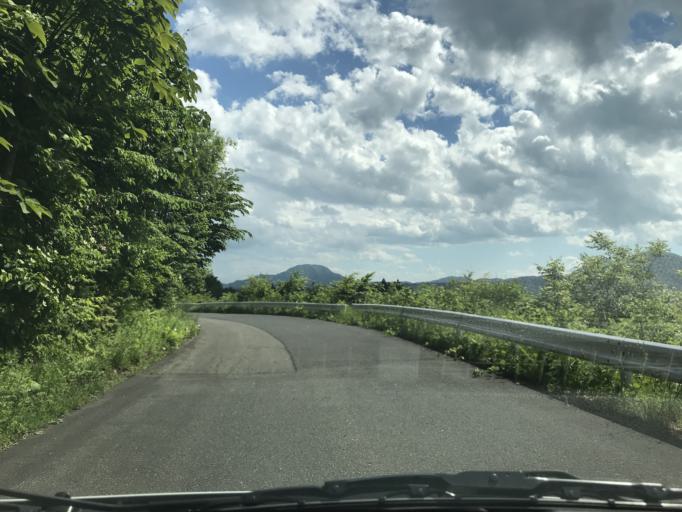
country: JP
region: Iwate
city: Ichinoseki
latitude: 38.8849
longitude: 140.9081
